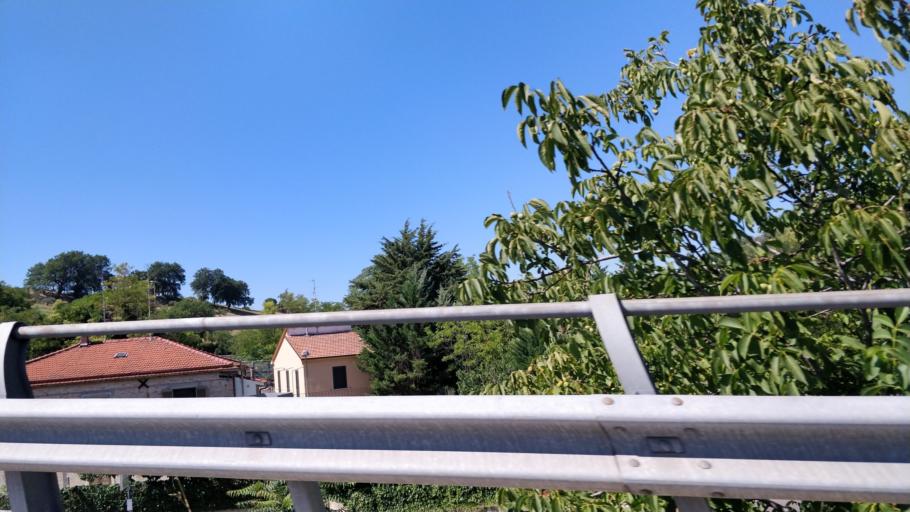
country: IT
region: Abruzzo
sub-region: Provincia di Chieti
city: Chieti
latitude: 42.3643
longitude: 14.1577
